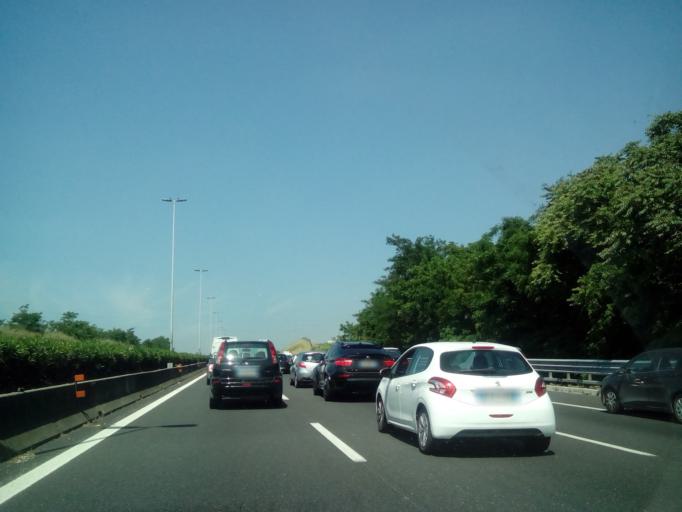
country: IT
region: Latium
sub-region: Citta metropolitana di Roma Capitale
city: Selcetta
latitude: 41.8001
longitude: 12.4606
